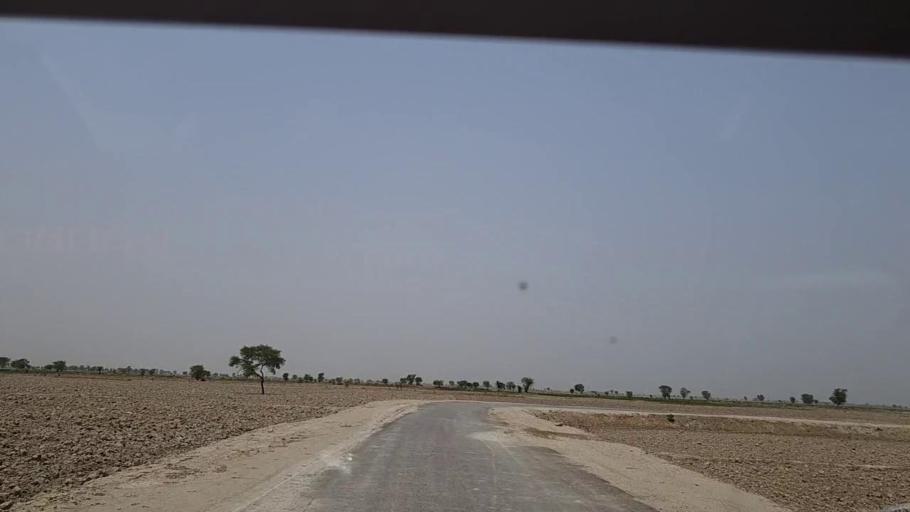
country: PK
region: Sindh
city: Khairpur Nathan Shah
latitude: 27.0179
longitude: 67.6319
